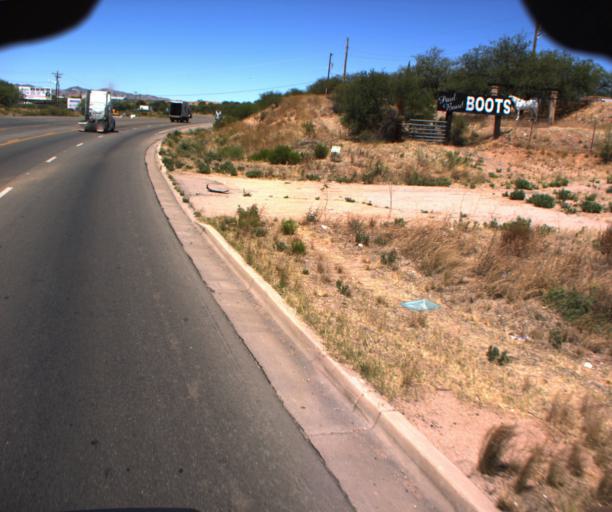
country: US
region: Arizona
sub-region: Santa Cruz County
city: Nogales
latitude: 31.3633
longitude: -110.9499
